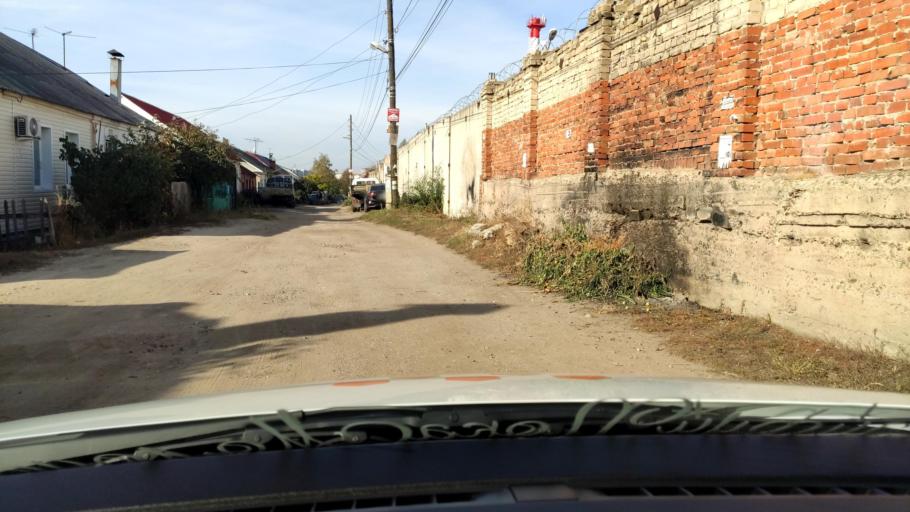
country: RU
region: Voronezj
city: Voronezh
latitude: 51.6695
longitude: 39.1561
